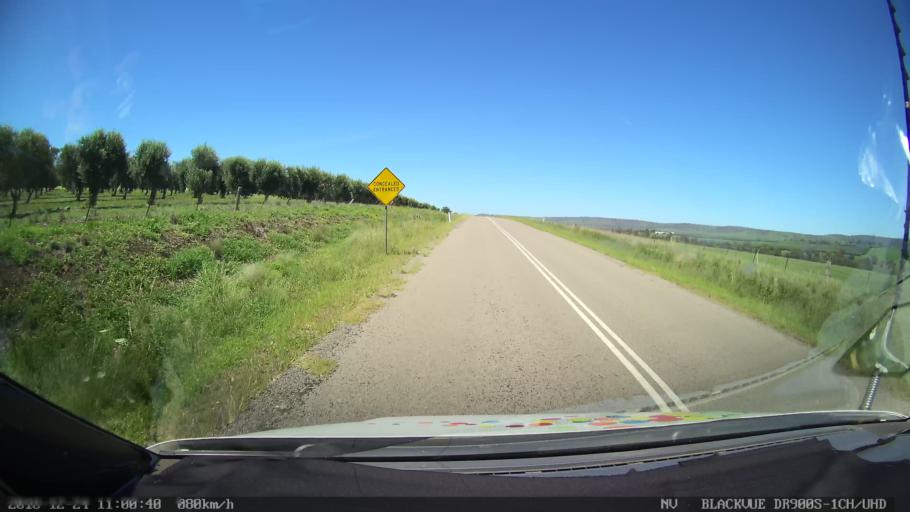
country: AU
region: New South Wales
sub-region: Upper Hunter Shire
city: Merriwa
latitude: -32.0700
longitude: 150.3924
